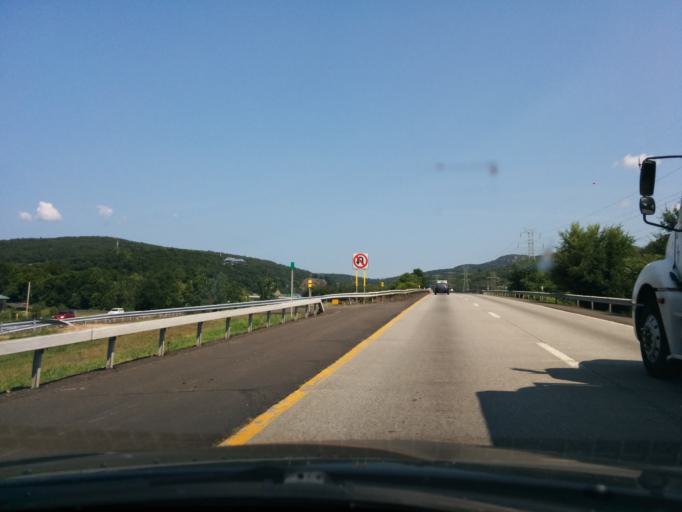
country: US
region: New York
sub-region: Rockland County
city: Suffern
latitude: 41.1186
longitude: -74.1618
